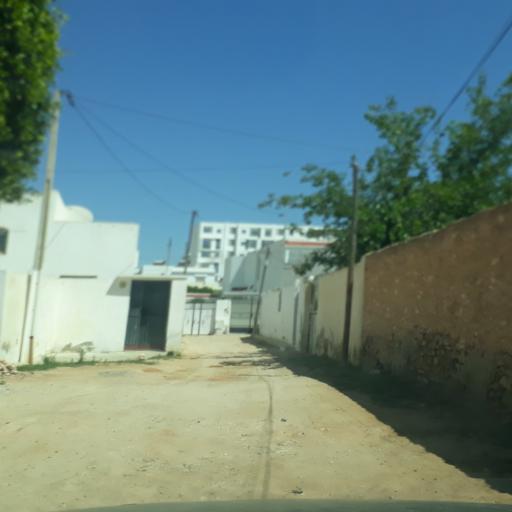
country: TN
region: Safaqis
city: Al Qarmadah
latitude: 34.7980
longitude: 10.7587
